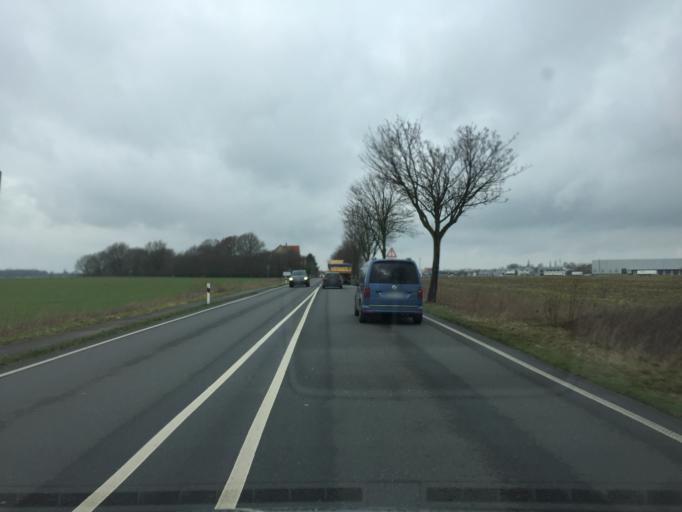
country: DE
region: Lower Saxony
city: Wunstorf
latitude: 52.4043
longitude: 9.4600
